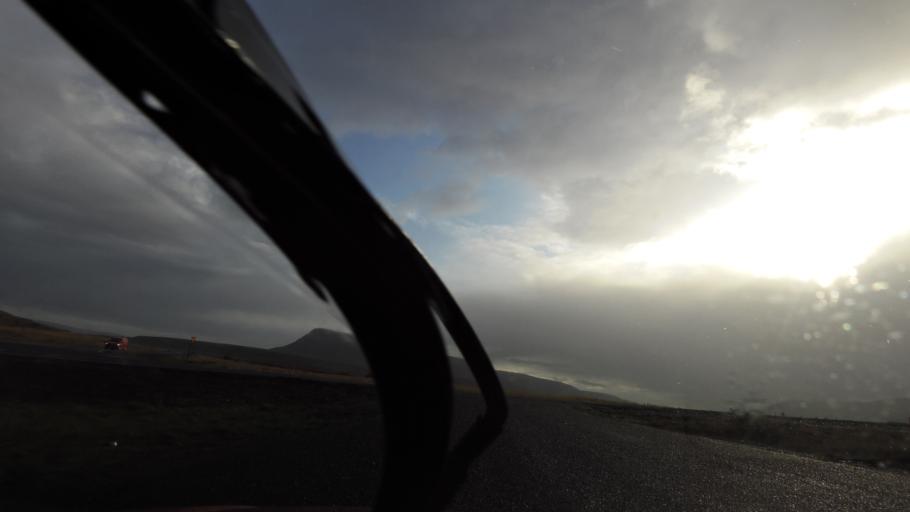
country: IS
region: West
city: Borgarnes
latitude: 64.5797
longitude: -21.6017
